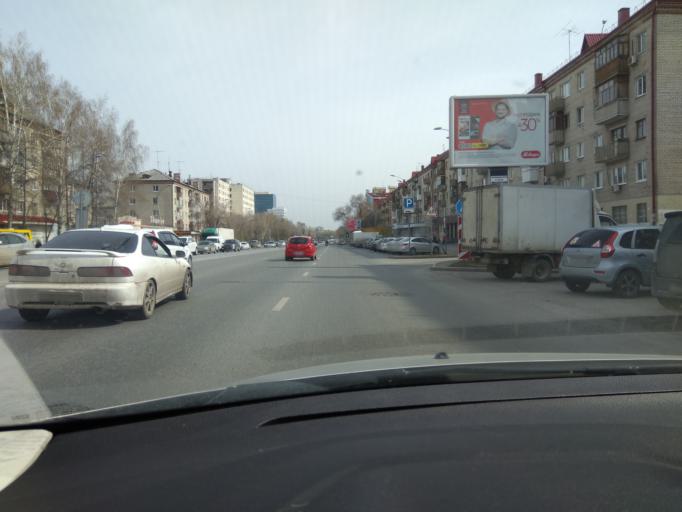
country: RU
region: Tjumen
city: Tyumen
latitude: 57.1403
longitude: 65.5733
